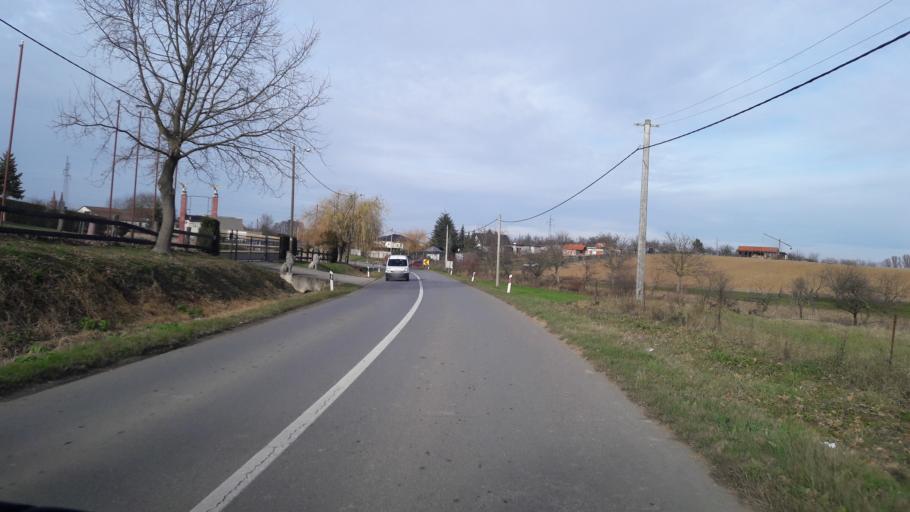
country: HR
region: Osjecko-Baranjska
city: Piskorevci
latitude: 45.2990
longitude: 18.4278
